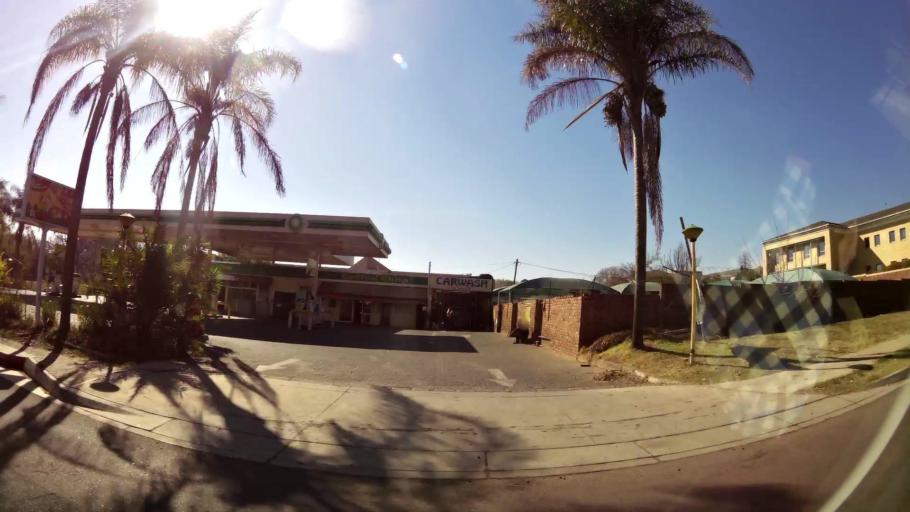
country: ZA
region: Gauteng
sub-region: City of Tshwane Metropolitan Municipality
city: Pretoria
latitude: -25.7716
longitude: 28.2237
